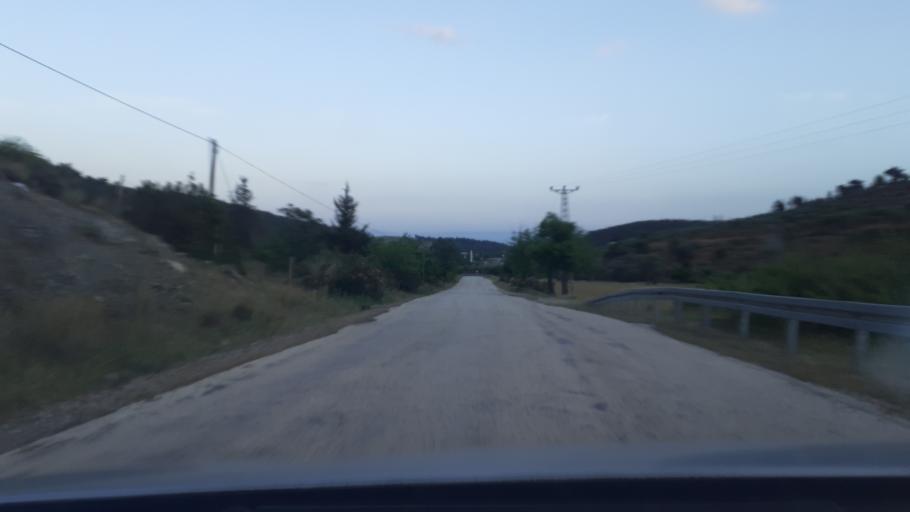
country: TR
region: Hatay
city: Kirikhan
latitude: 36.5118
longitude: 36.3199
